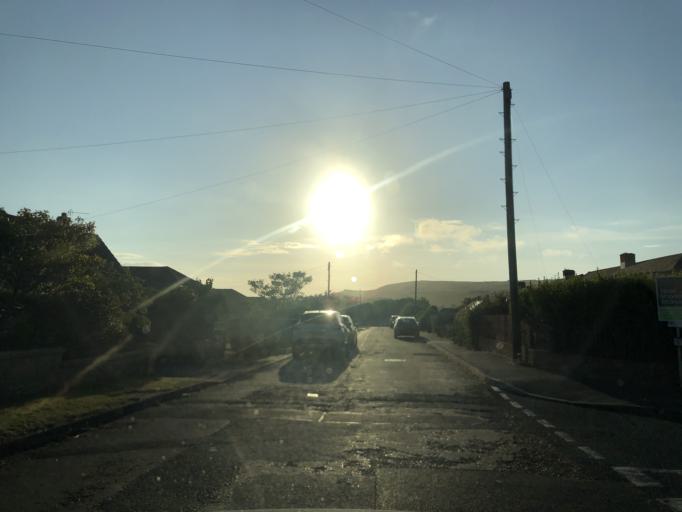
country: GB
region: England
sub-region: Isle of Wight
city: Chale
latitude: 50.6410
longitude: -1.3550
